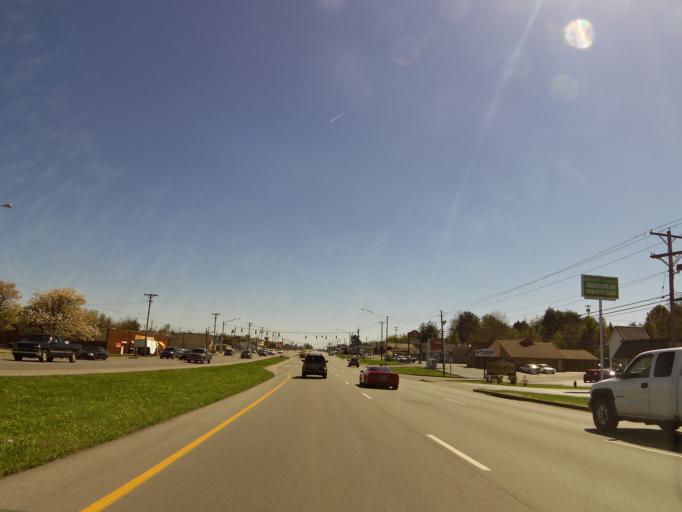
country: US
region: Kentucky
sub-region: Pulaski County
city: Somerset
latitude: 37.0833
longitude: -84.6169
